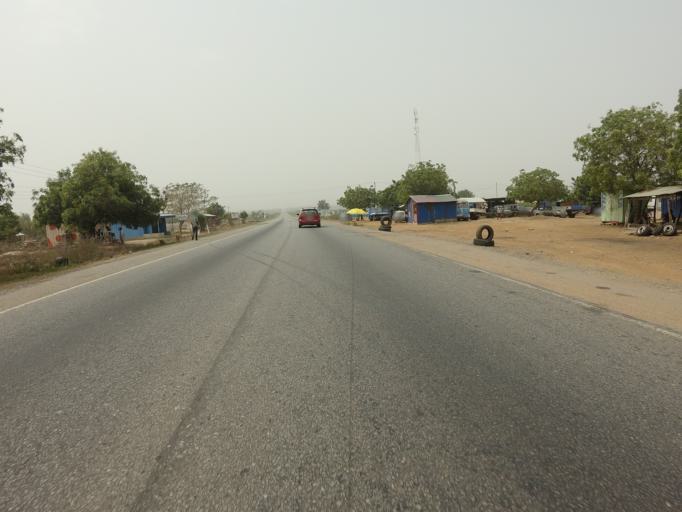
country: GH
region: Greater Accra
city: Tema
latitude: 5.8656
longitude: 0.2889
